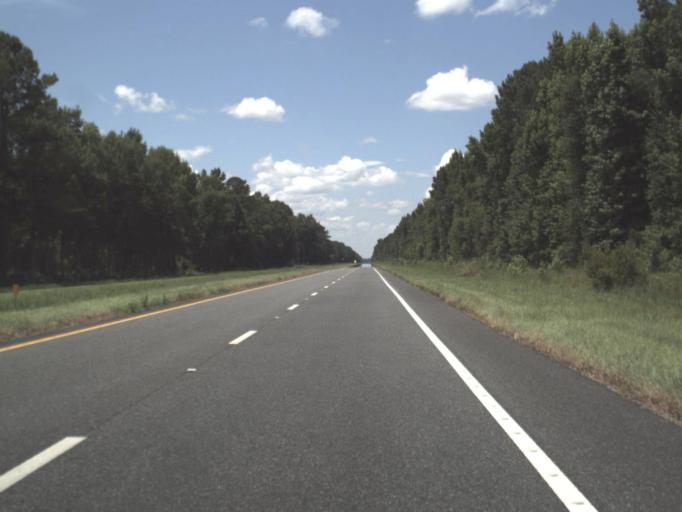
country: US
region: Florida
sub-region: Taylor County
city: Perry
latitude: 30.2726
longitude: -83.7202
